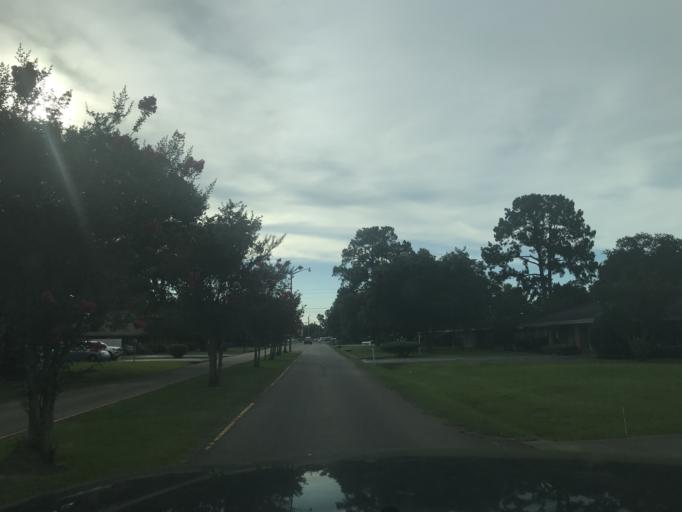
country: US
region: Louisiana
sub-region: Lafayette Parish
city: Lafayette
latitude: 30.1952
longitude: -92.0555
